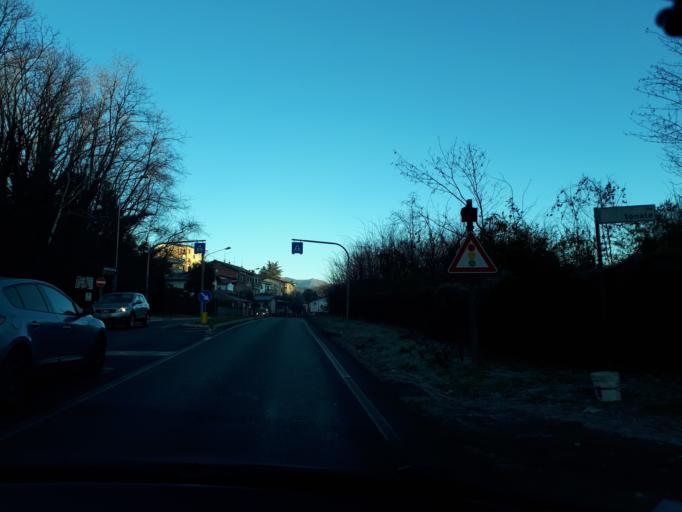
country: IT
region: Lombardy
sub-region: Provincia di Como
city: Grandate
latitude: 45.7743
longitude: 9.0645
